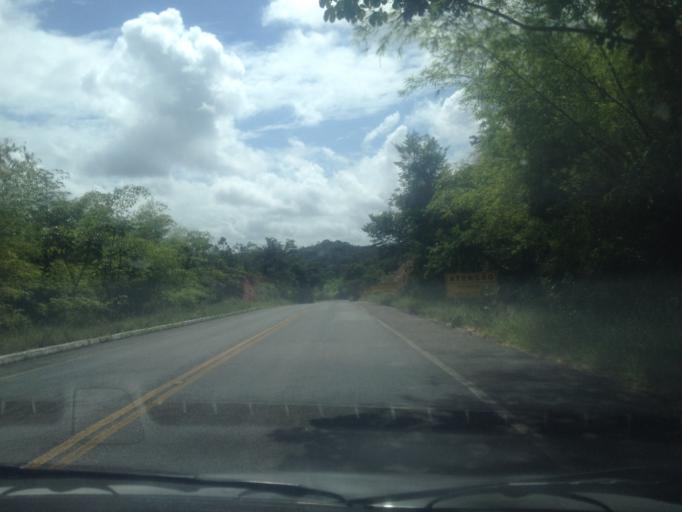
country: BR
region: Bahia
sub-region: Conde
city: Conde
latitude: -12.0427
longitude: -37.7061
